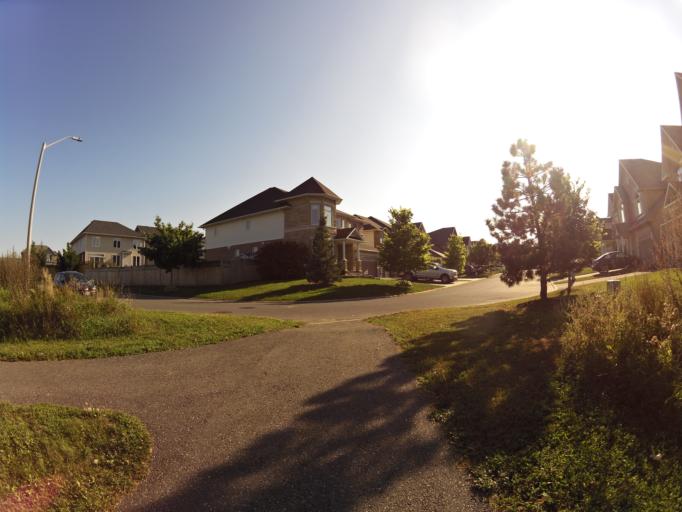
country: CA
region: Ontario
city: Bells Corners
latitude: 45.3485
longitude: -75.9459
